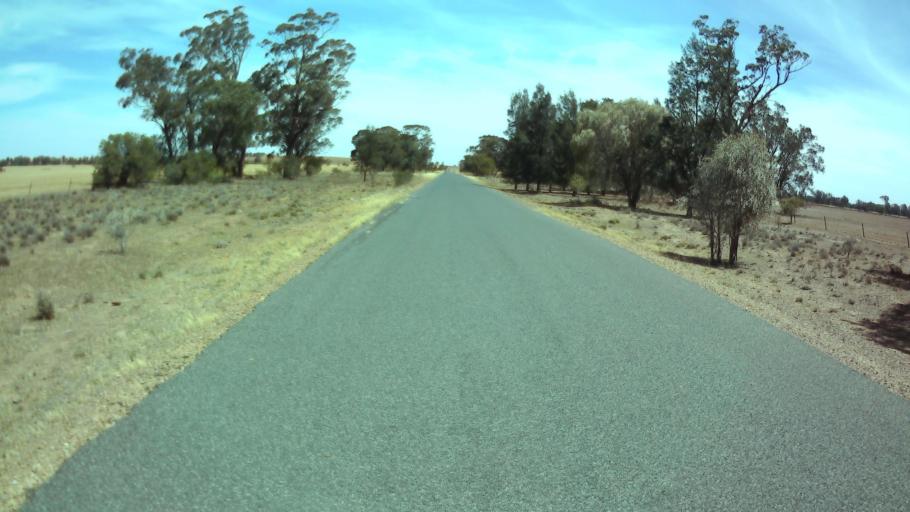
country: AU
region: New South Wales
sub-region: Weddin
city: Grenfell
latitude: -33.8811
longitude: 147.7429
